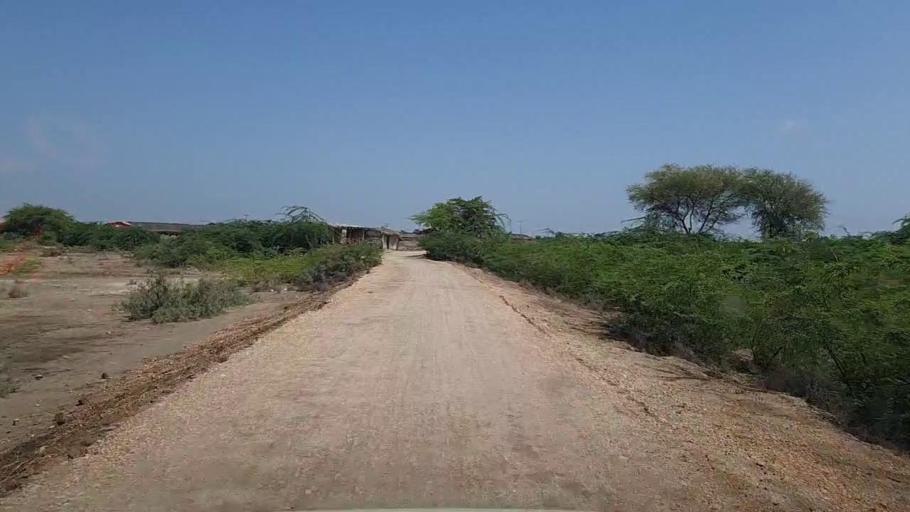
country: PK
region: Sindh
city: Talhar
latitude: 24.8365
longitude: 68.7153
